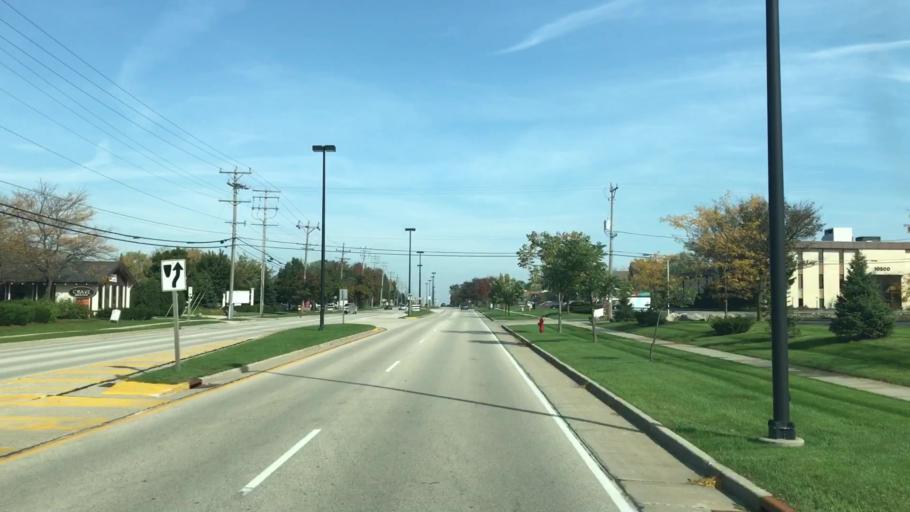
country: US
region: Wisconsin
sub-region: Milwaukee County
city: River Hills
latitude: 43.2076
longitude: -87.9242
